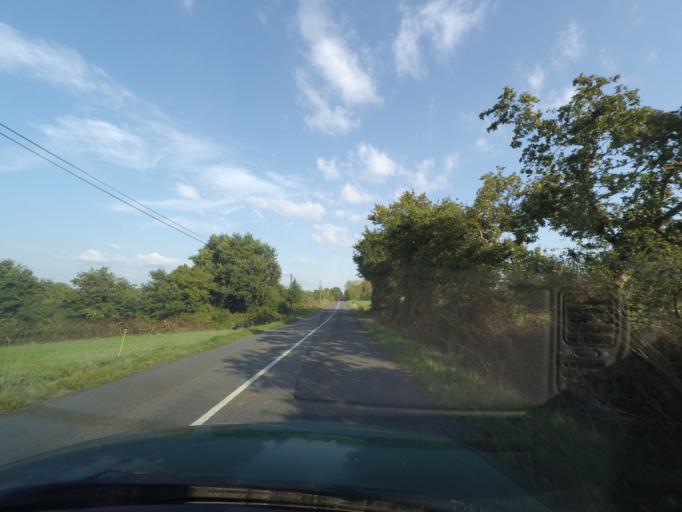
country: FR
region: Pays de la Loire
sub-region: Departement de la Loire-Atlantique
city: Saint-Philbert-de-Grand-Lieu
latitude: 47.0257
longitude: -1.6163
